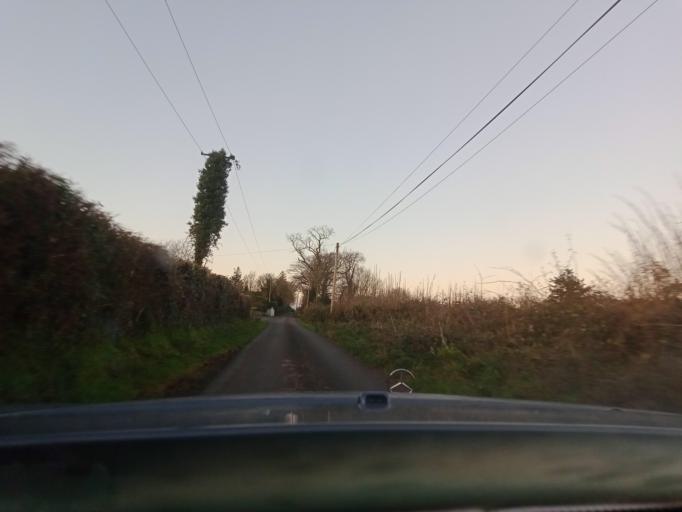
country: IE
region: Leinster
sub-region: Kilkenny
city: Graiguenamanagh
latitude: 52.5520
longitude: -6.9617
